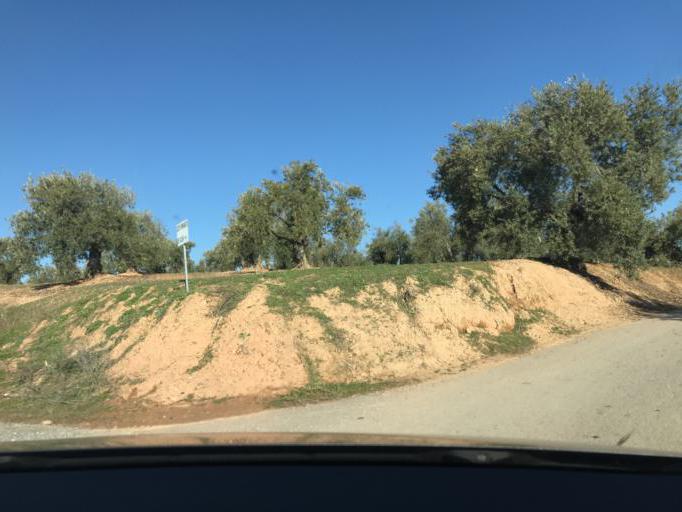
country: ES
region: Andalusia
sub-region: Provincia de Granada
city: Peligros
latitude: 37.2432
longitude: -3.6255
